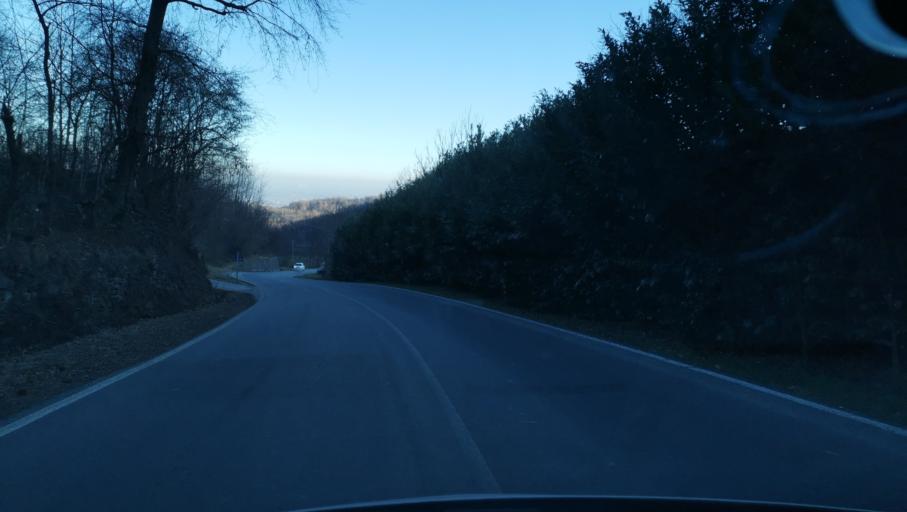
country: IT
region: Piedmont
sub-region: Provincia di Cuneo
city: Bagnolo Piemonte
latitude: 44.7500
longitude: 7.2669
